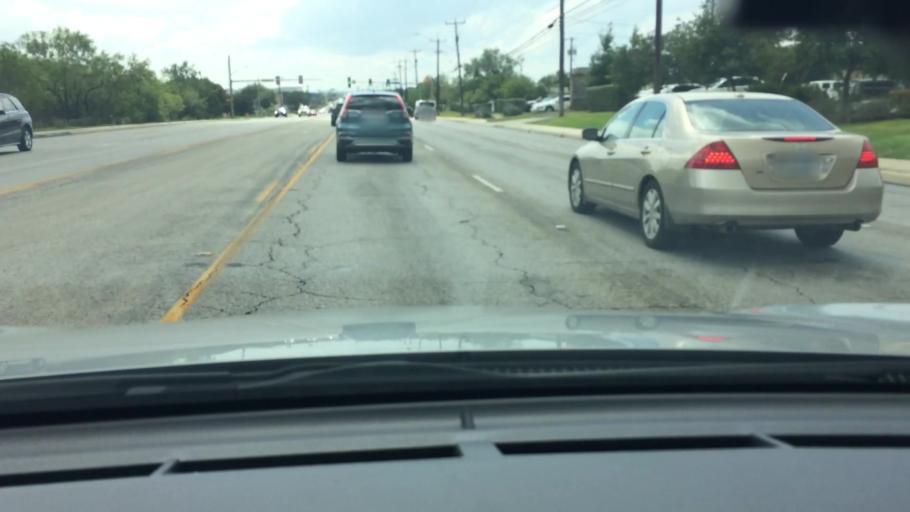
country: US
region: Texas
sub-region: Bexar County
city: Leon Valley
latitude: 29.5371
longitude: -98.5866
